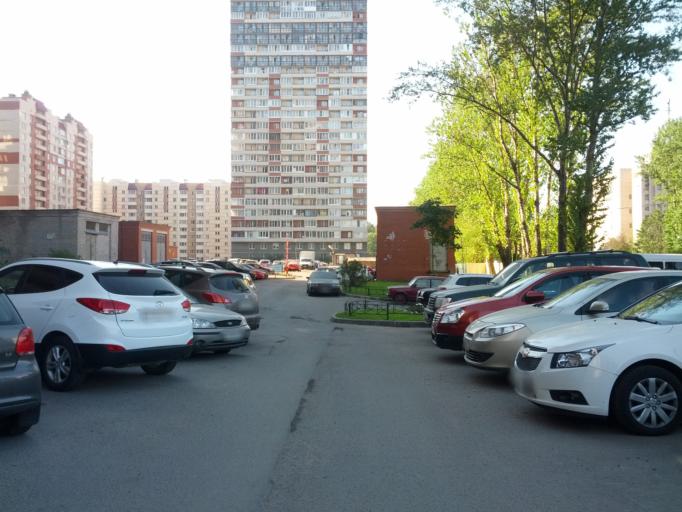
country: RU
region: St.-Petersburg
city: Kupchino
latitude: 59.8403
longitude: 30.3552
